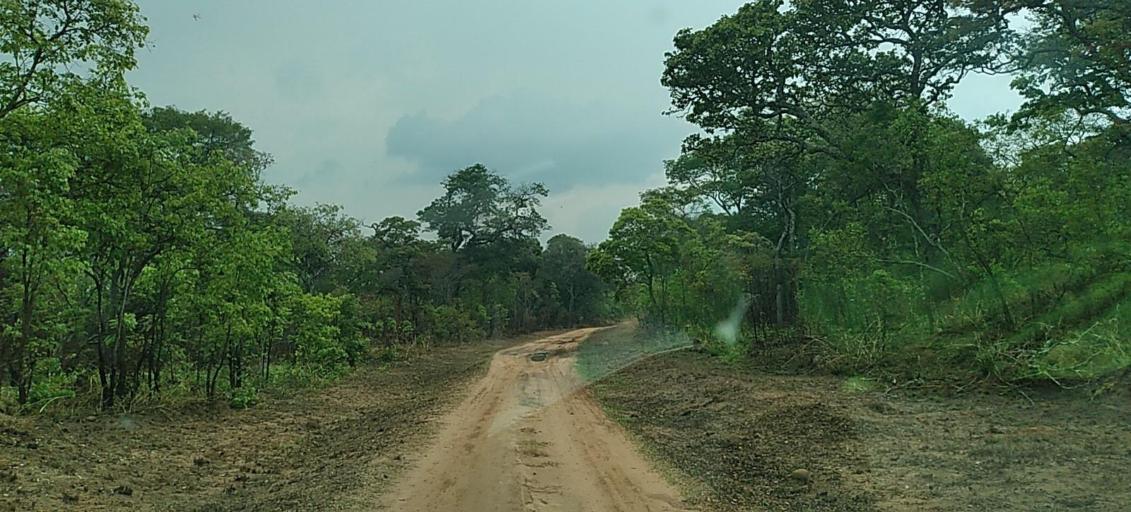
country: ZM
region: North-Western
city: Mwinilunga
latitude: -11.4699
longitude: 24.4617
